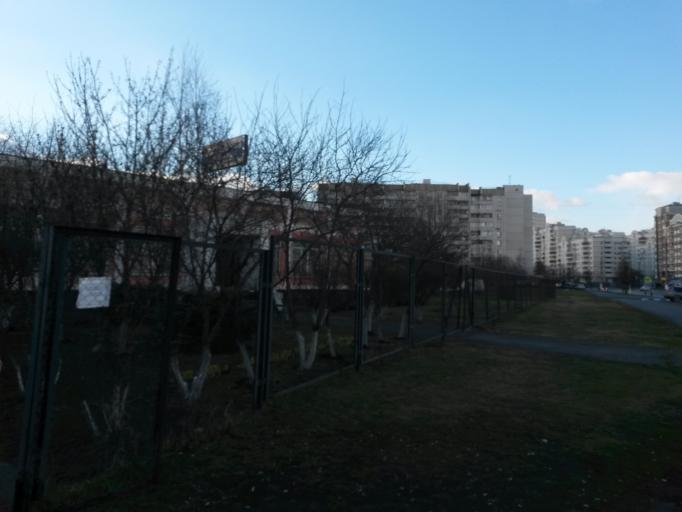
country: RU
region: Moskovskaya
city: Shcherbinka
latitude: 55.5420
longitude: 37.5578
